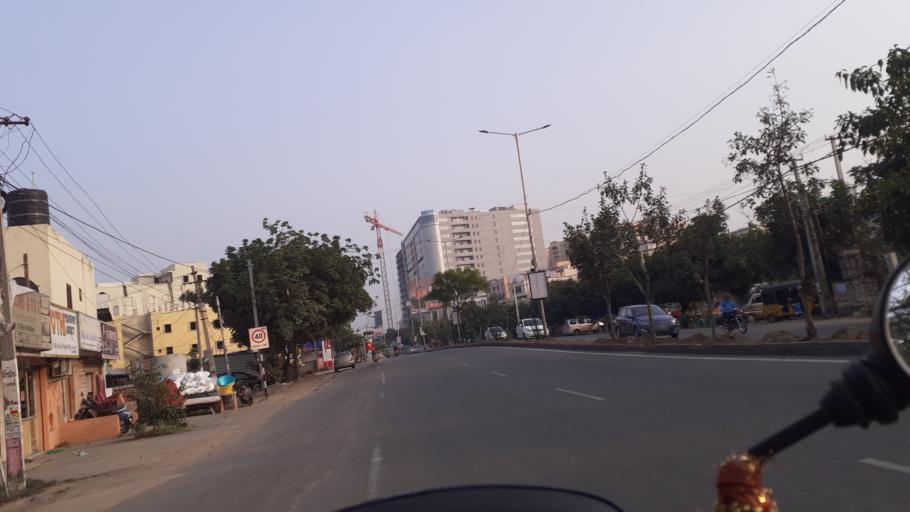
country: IN
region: Telangana
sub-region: Medak
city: Serilingampalle
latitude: 17.4879
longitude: 78.3560
